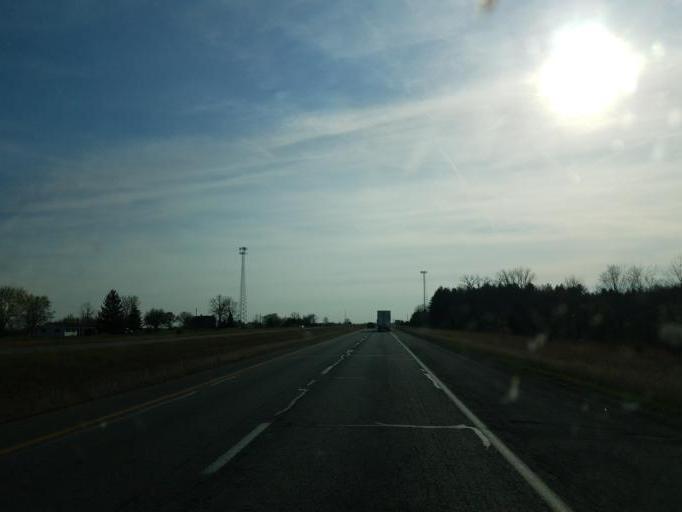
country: US
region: Ohio
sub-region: Madison County
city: Mount Sterling
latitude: 39.7836
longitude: -83.2515
